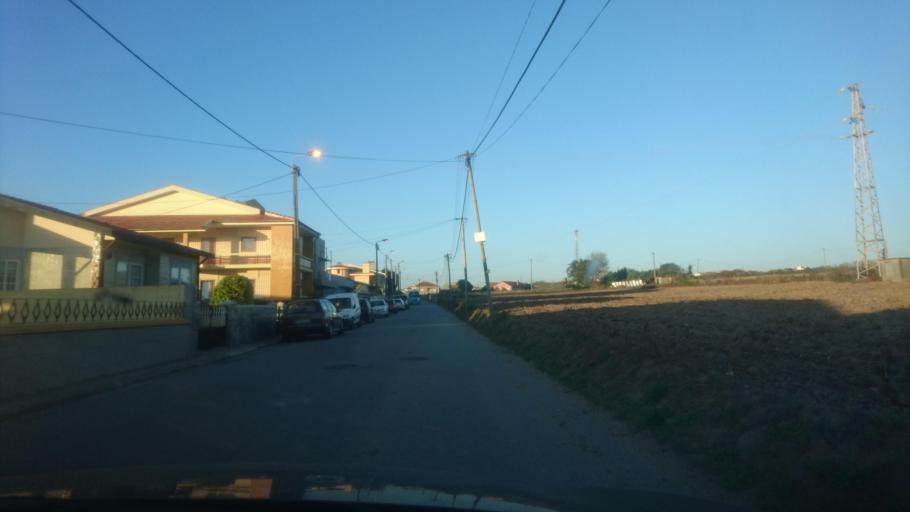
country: PT
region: Porto
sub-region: Matosinhos
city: Lavra
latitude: 41.2632
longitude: -8.7171
